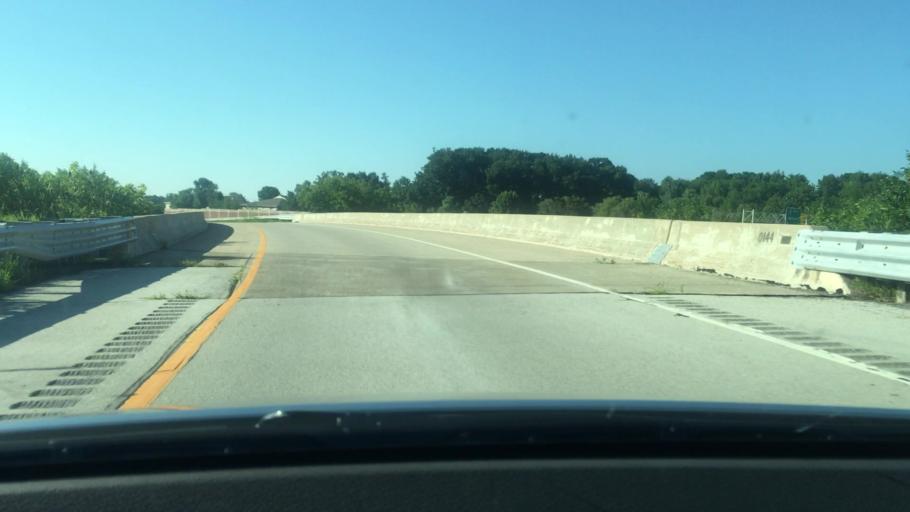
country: US
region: Wisconsin
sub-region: Brown County
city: Ashwaubenon
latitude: 44.4823
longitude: -88.0774
